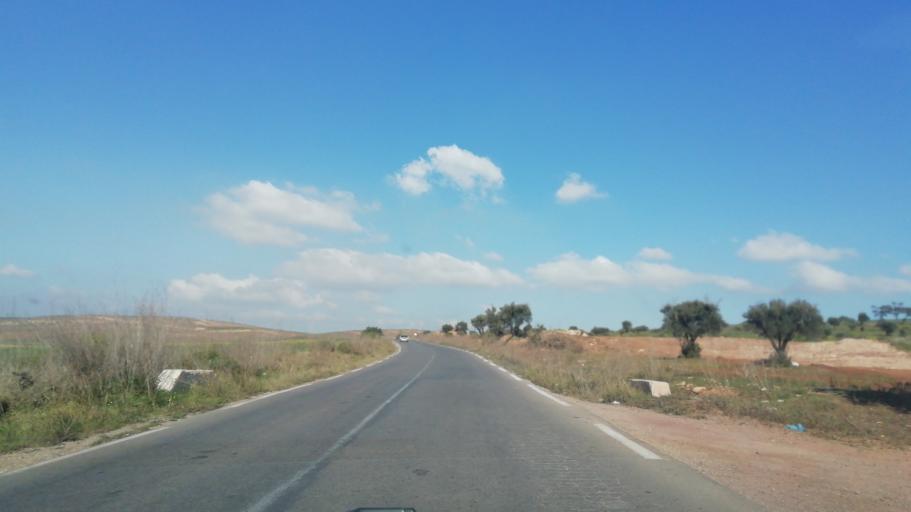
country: DZ
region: Oran
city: Ain el Bya
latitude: 35.7385
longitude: -0.2545
